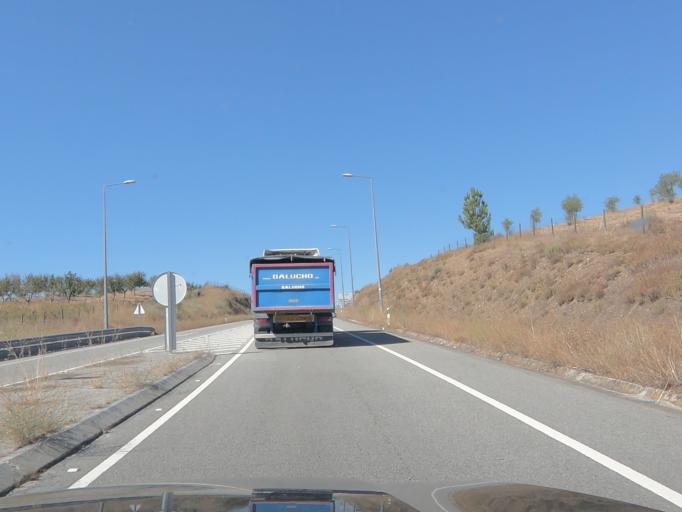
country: PT
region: Braganca
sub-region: Mirandela
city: Mirandela
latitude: 41.5403
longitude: -7.2540
